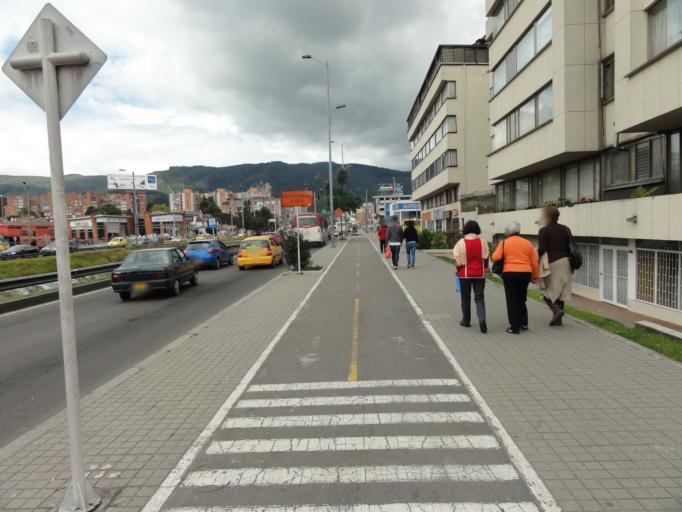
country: CO
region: Bogota D.C.
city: Barrio San Luis
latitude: 4.7055
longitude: -74.0493
